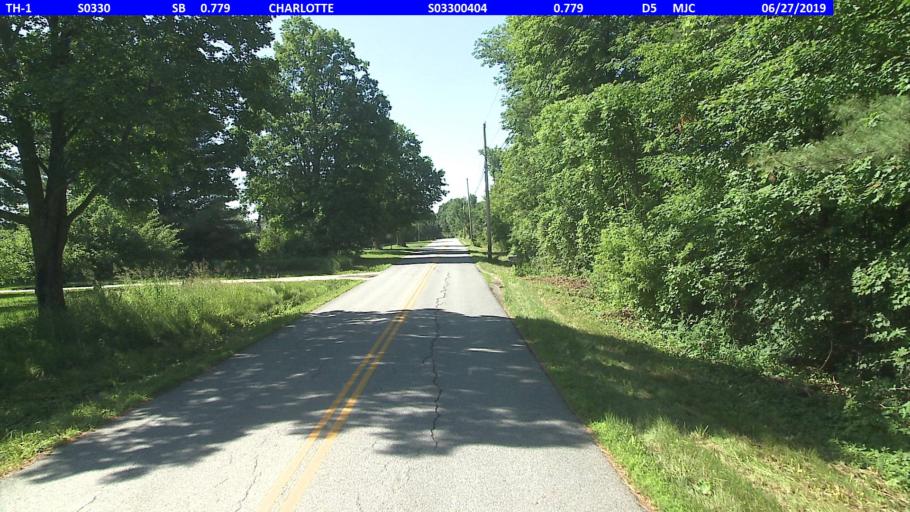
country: US
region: Vermont
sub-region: Chittenden County
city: Hinesburg
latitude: 44.3307
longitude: -73.1917
